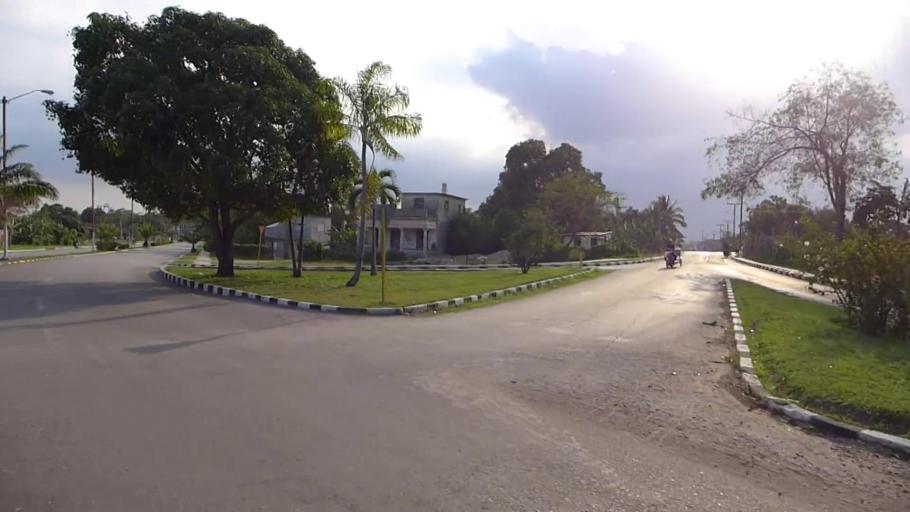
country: CU
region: Camaguey
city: Camaguey
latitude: 21.3826
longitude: -77.9078
